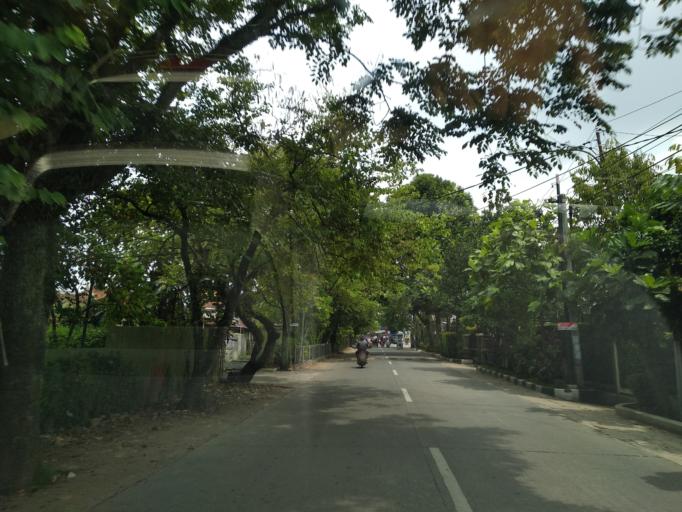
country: ID
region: West Java
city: Bandung
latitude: -6.9459
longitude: 107.6335
